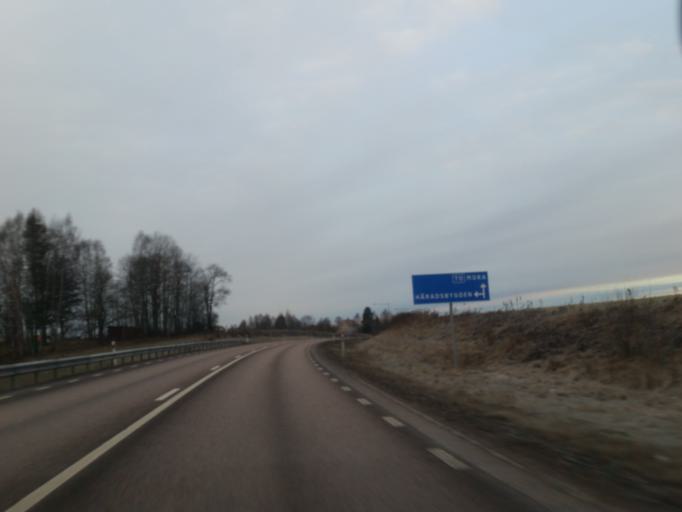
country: SE
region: Dalarna
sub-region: Leksand Municipality
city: Smedby
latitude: 60.6970
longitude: 15.0575
